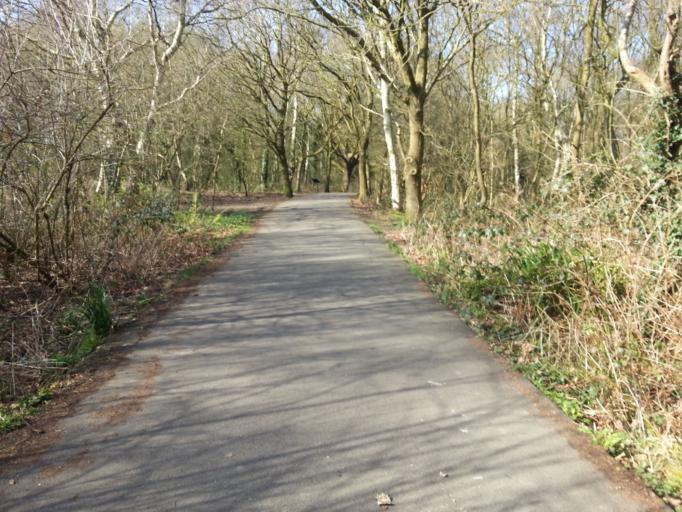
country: GB
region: England
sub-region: Knowsley
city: Huyton
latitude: 53.3658
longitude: -2.8410
